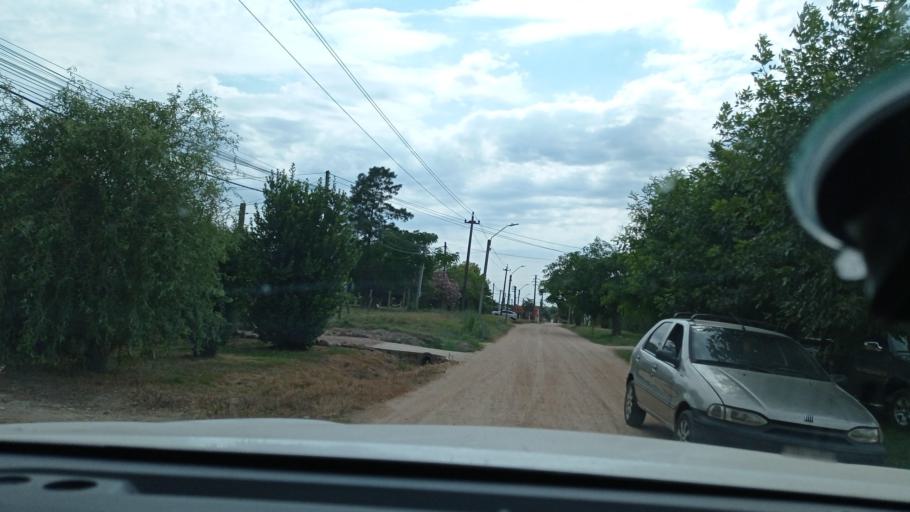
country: UY
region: Canelones
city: Pando
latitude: -34.7062
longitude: -55.9673
